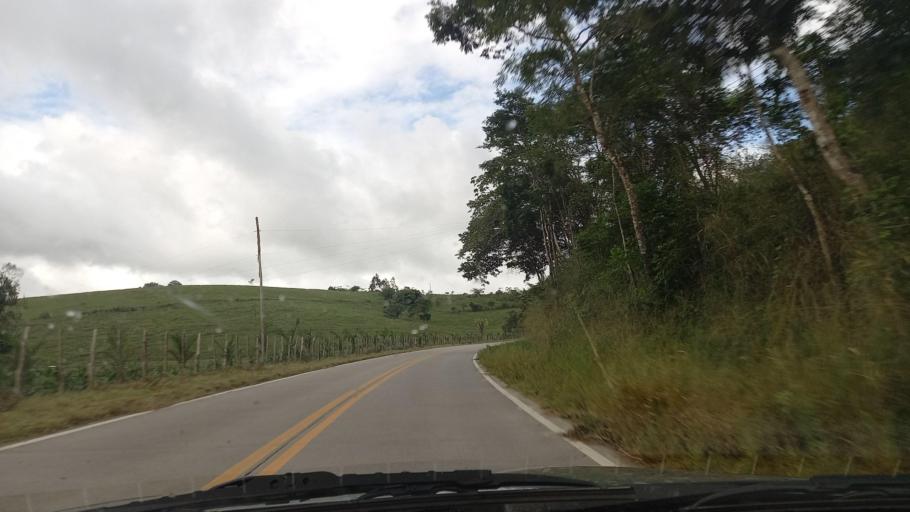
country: BR
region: Pernambuco
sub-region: Quipapa
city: Quipapa
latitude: -8.7875
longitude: -35.9702
